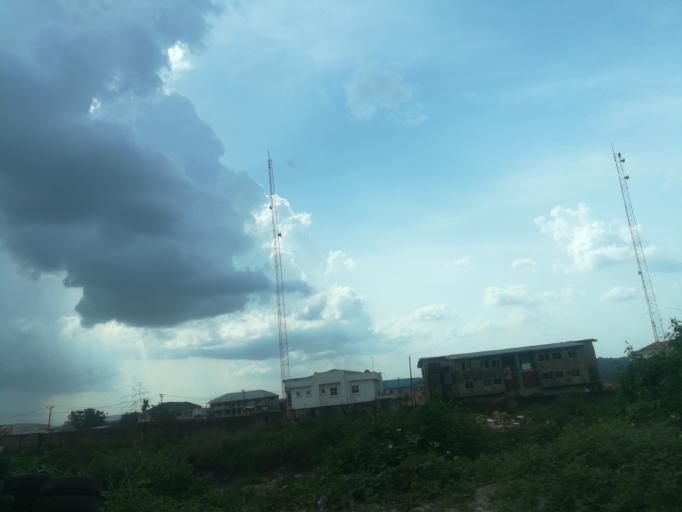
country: NG
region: Oyo
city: Moniya
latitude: 7.4725
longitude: 3.9146
